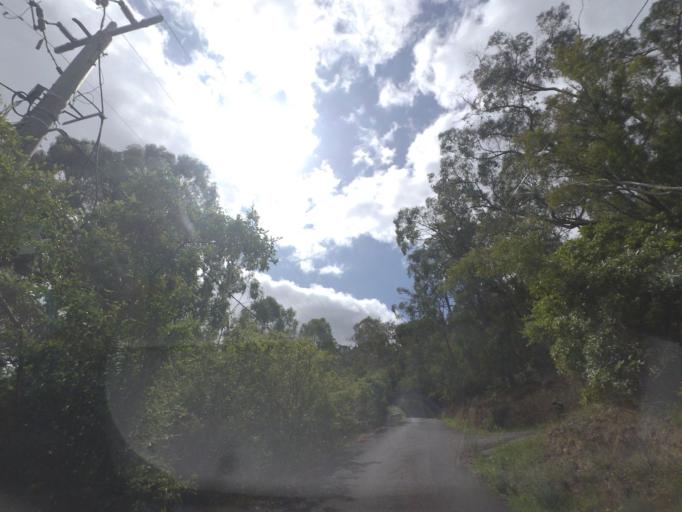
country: AU
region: Victoria
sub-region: Manningham
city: Park Orchards
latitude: -37.7861
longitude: 145.2004
